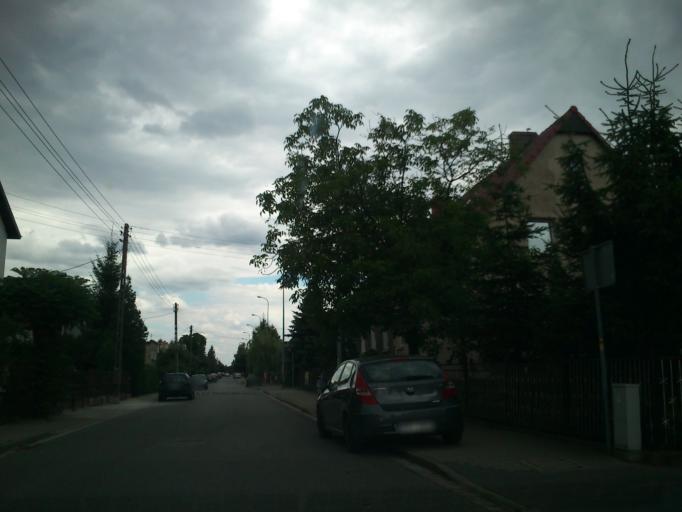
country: PL
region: Lower Silesian Voivodeship
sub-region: Powiat wroclawski
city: Smolec
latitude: 51.1581
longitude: 16.8983
